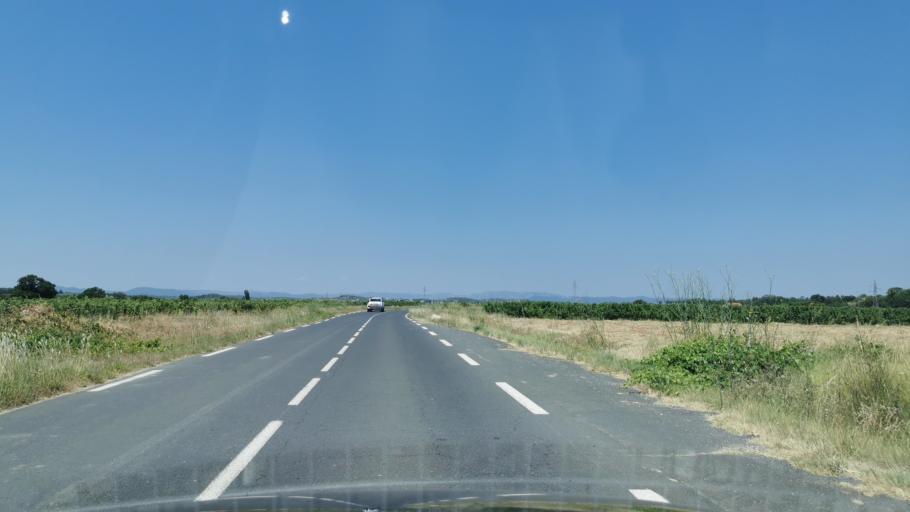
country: FR
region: Languedoc-Roussillon
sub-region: Departement de l'Herault
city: Maureilhan
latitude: 43.3665
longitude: 3.1161
